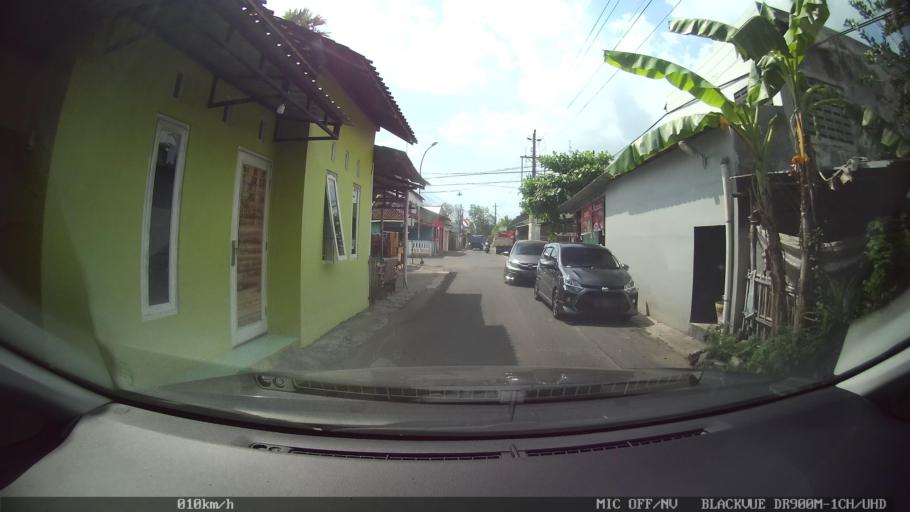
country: ID
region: Daerah Istimewa Yogyakarta
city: Kasihan
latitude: -7.8129
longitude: 110.3367
